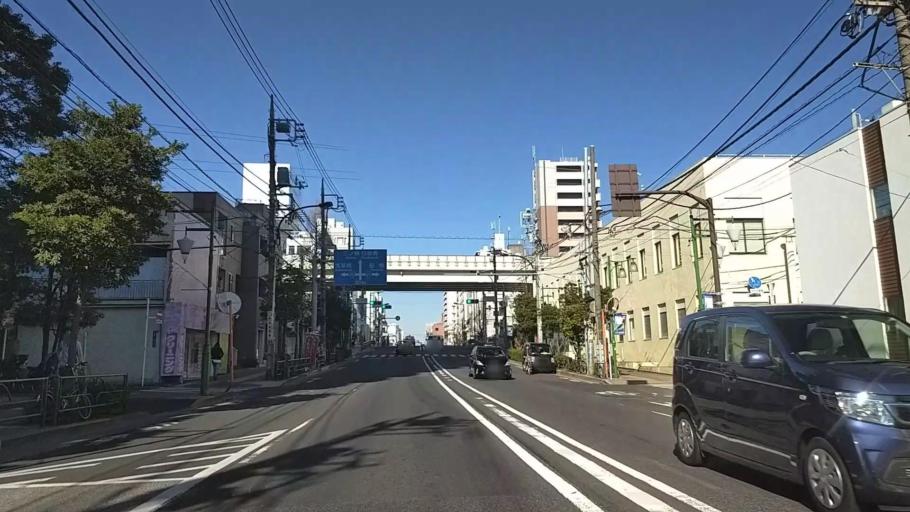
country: JP
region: Tokyo
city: Urayasu
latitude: 35.6927
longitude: 139.8261
